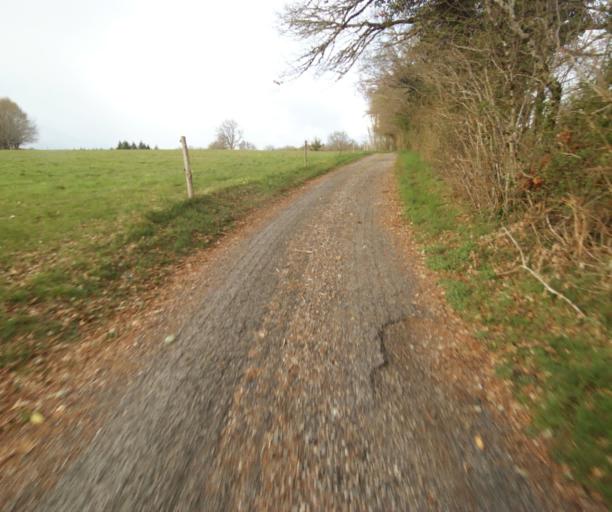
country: FR
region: Limousin
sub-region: Departement de la Correze
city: Argentat
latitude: 45.2109
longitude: 1.9907
